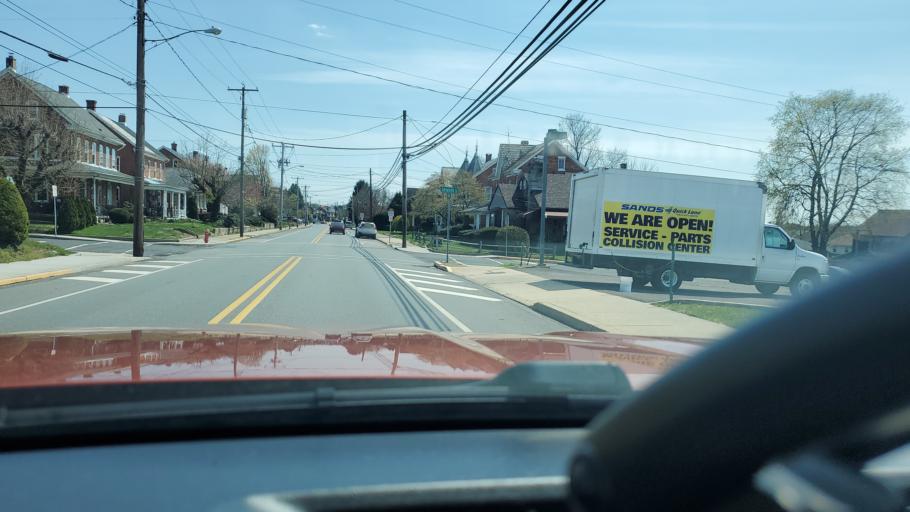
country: US
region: Pennsylvania
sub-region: Montgomery County
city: Red Hill
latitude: 40.3796
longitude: -75.4847
